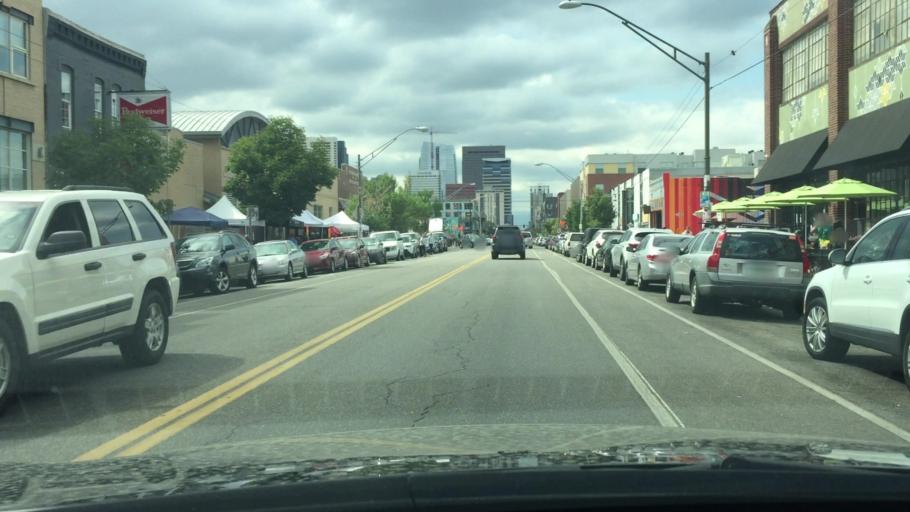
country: US
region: Colorado
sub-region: Denver County
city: Denver
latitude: 39.7594
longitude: -104.9843
